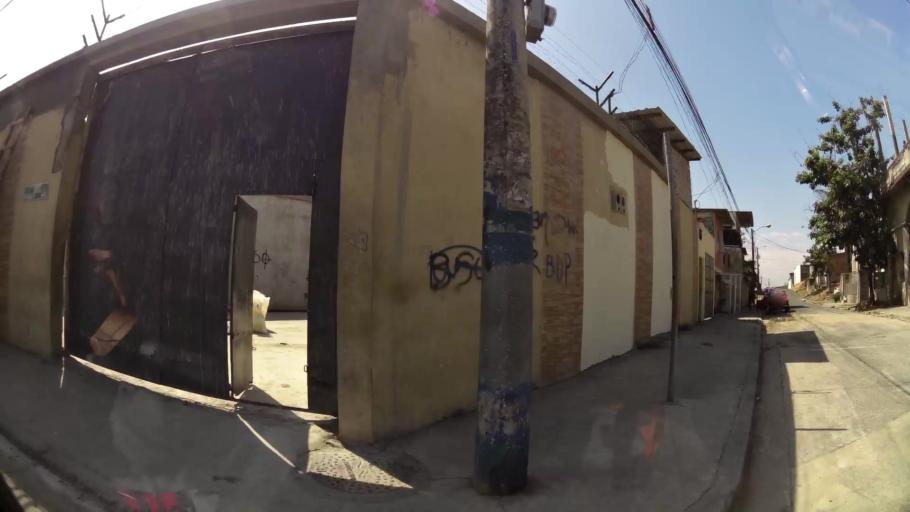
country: EC
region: Guayas
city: Eloy Alfaro
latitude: -2.1211
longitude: -79.9117
